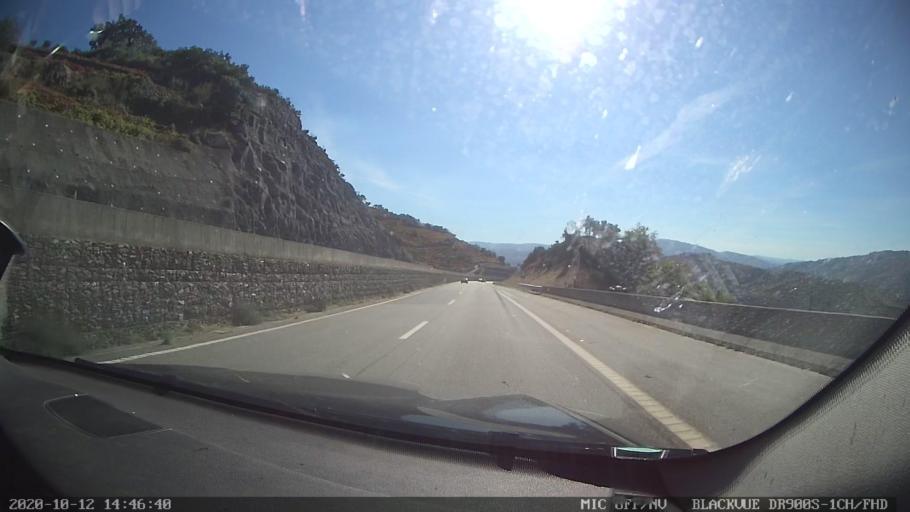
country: PT
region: Vila Real
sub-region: Peso da Regua
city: Peso da Regua
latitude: 41.2011
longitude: -7.7464
